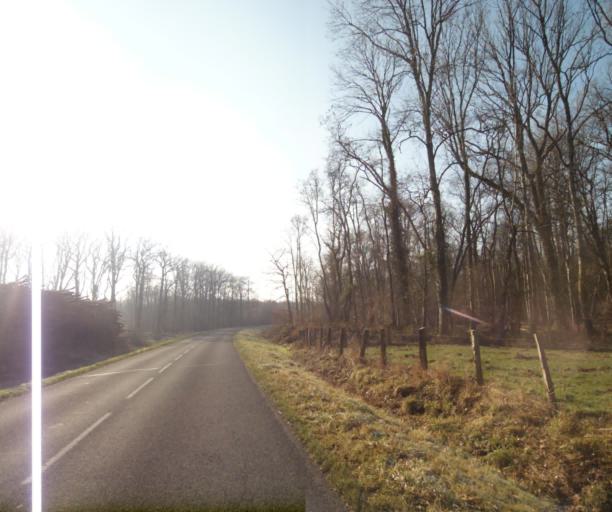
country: FR
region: Champagne-Ardenne
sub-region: Departement de la Haute-Marne
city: Wassy
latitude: 48.4817
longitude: 4.9339
